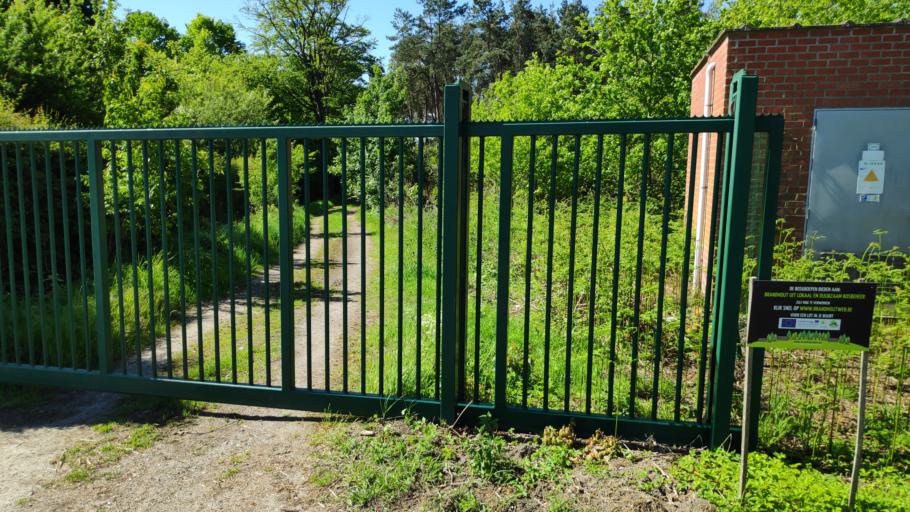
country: BE
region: Flanders
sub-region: Provincie Oost-Vlaanderen
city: Zomergem
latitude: 51.1313
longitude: 3.5159
